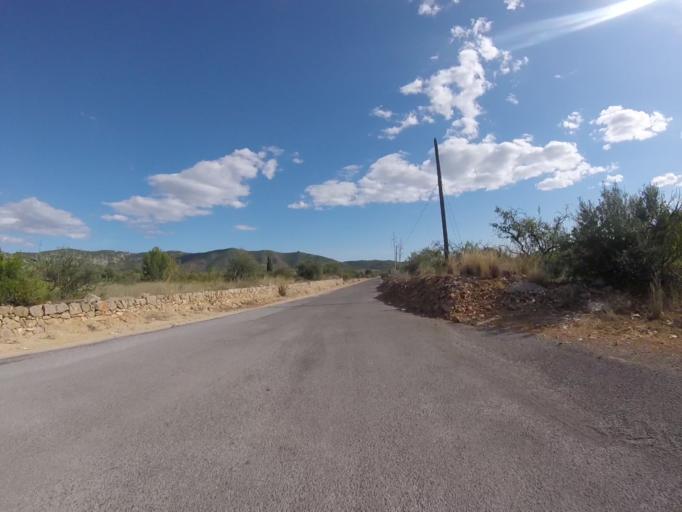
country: ES
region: Valencia
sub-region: Provincia de Castello
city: Alcala de Xivert
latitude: 40.2725
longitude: 0.2364
